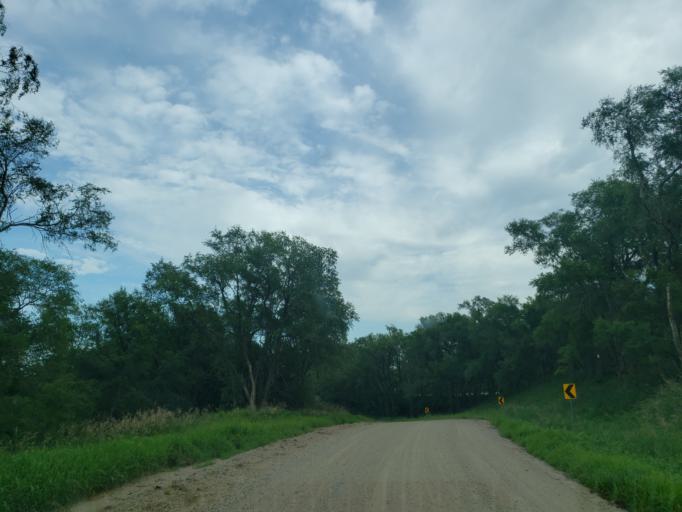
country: US
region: South Dakota
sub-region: Davison County
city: Mitchell
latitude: 43.6878
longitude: -97.9806
